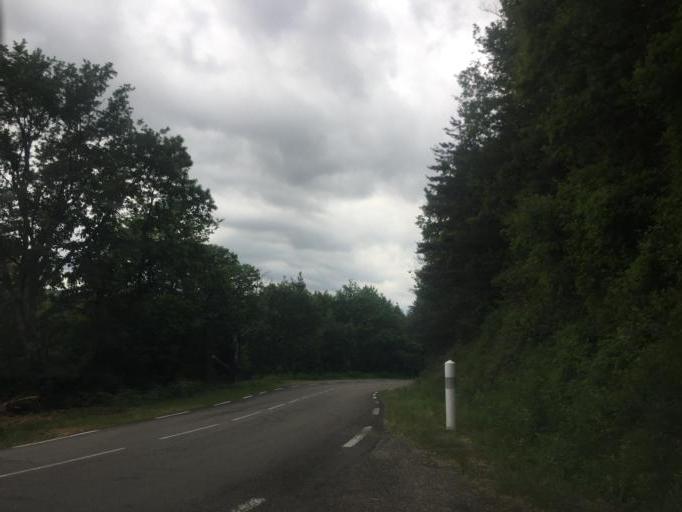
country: FR
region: Rhone-Alpes
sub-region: Departement de l'Ardeche
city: Privas
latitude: 44.7643
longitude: 4.5853
